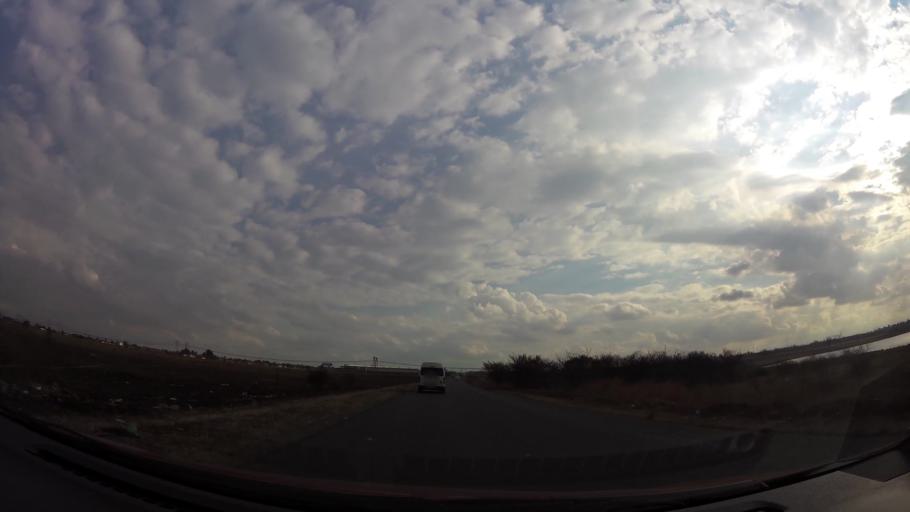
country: ZA
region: Gauteng
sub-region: Sedibeng District Municipality
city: Vereeniging
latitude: -26.6938
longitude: 27.8939
